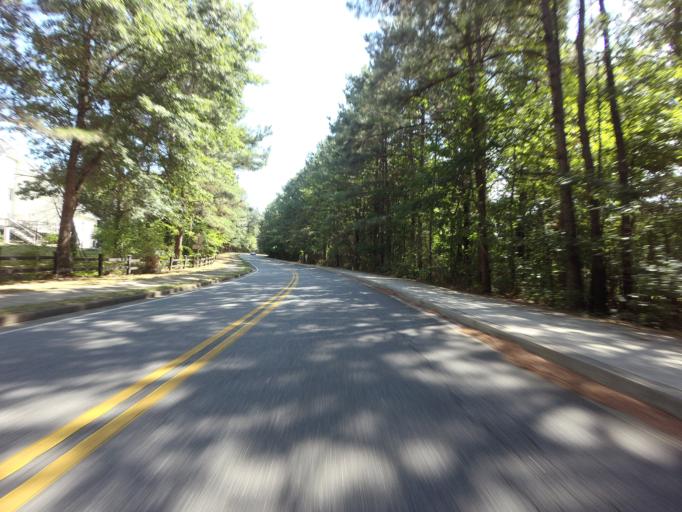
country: US
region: Georgia
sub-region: Fulton County
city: Johns Creek
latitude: 34.0624
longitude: -84.1814
